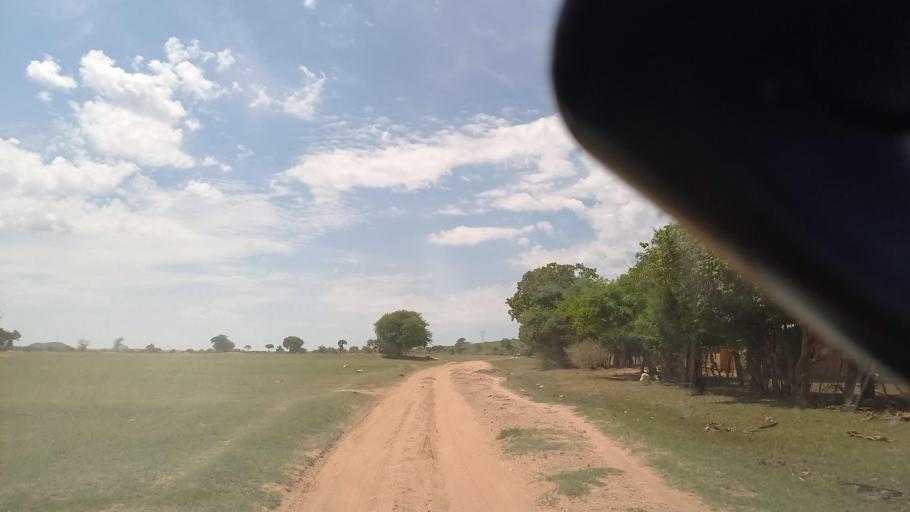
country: ZM
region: Southern
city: Mazabuka
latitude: -16.1514
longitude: 27.7791
